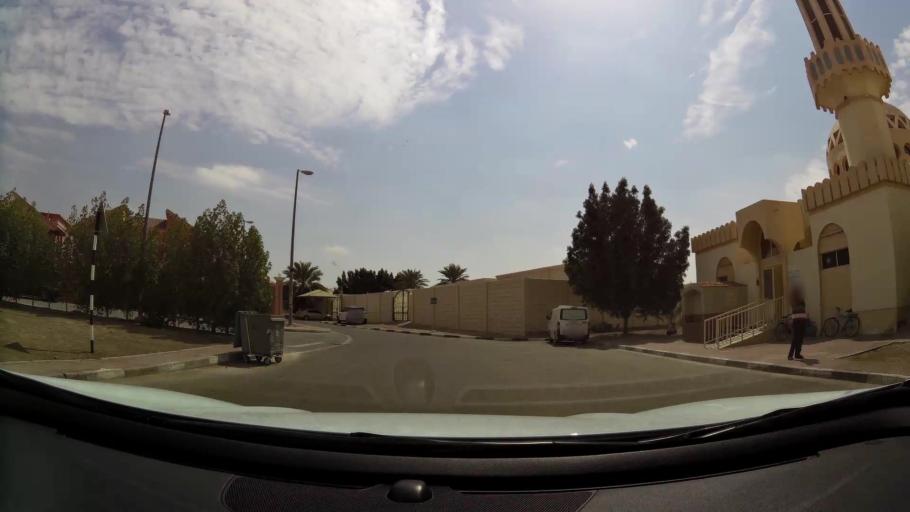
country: AE
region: Abu Dhabi
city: Al Ain
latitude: 24.1970
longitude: 55.7880
